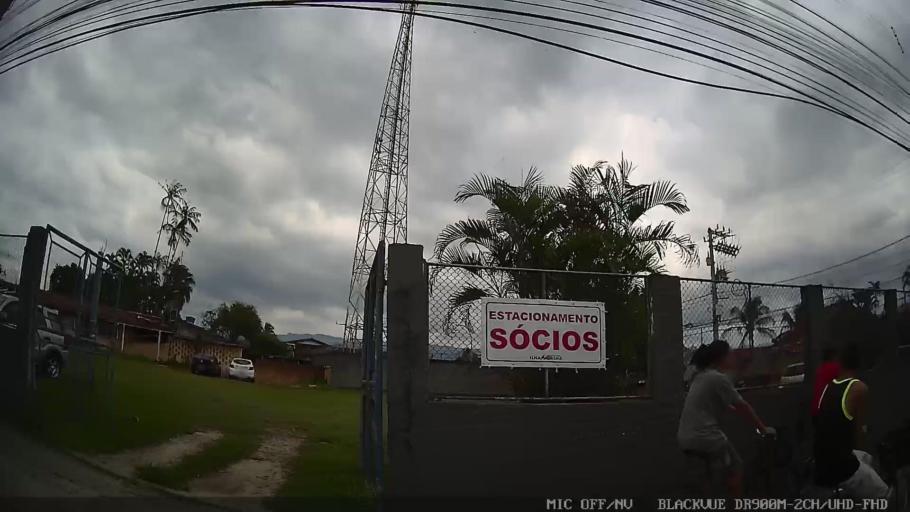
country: BR
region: Sao Paulo
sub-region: Caraguatatuba
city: Caraguatatuba
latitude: -23.6770
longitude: -45.4448
